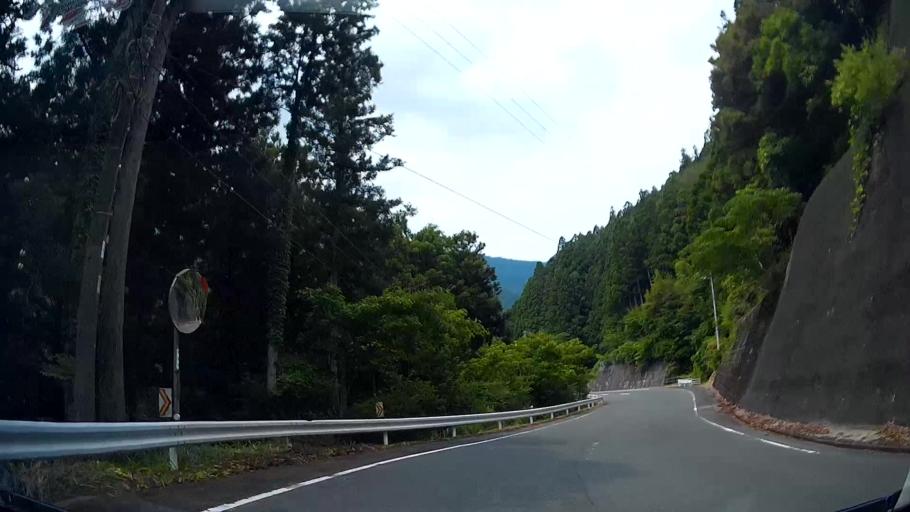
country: JP
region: Shizuoka
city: Mori
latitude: 35.0832
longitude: 137.8294
